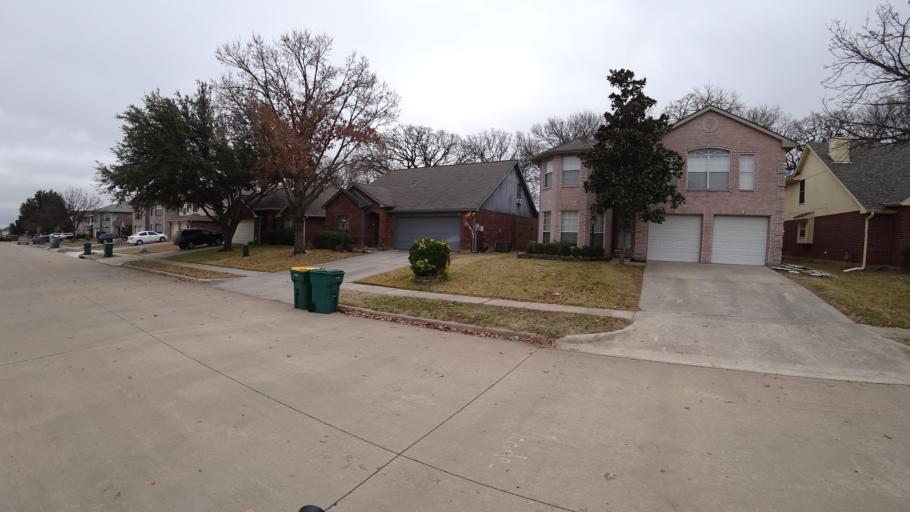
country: US
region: Texas
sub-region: Denton County
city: Lewisville
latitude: 33.0245
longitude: -97.0334
